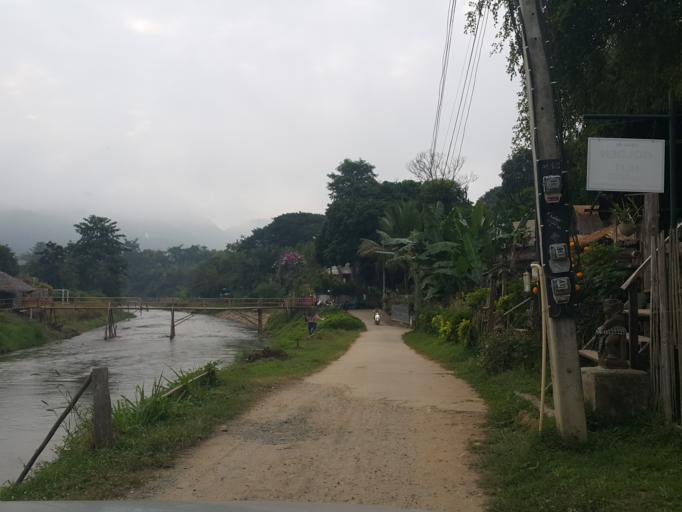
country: TH
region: Chiang Mai
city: Pai
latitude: 19.3609
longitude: 98.4437
